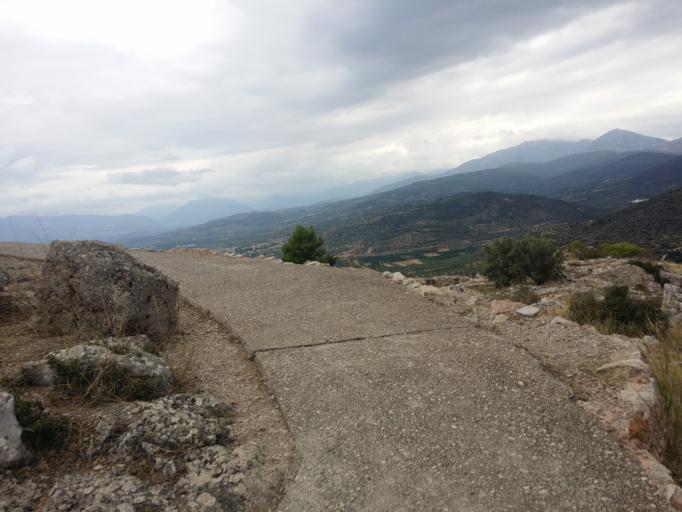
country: GR
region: Peloponnese
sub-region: Nomos Argolidos
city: Koutsopodi
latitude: 37.7308
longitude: 22.7575
